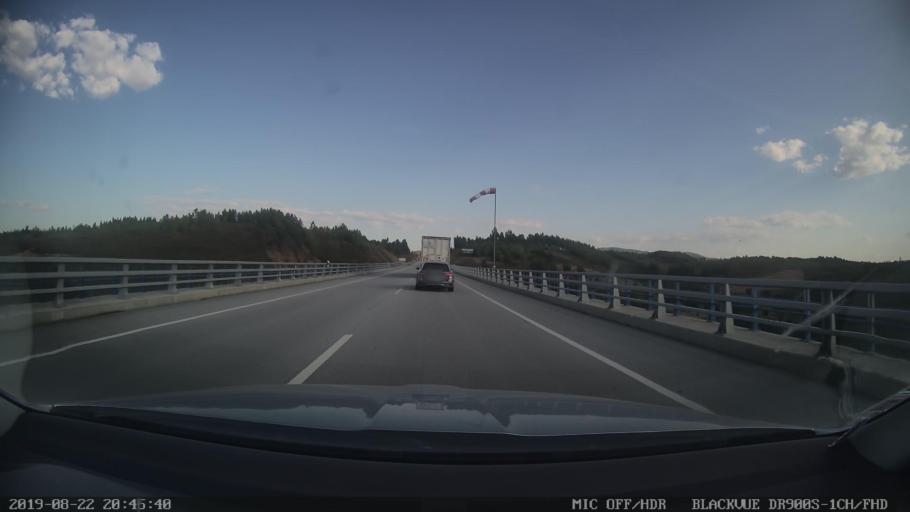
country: PT
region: Castelo Branco
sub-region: Proenca-A-Nova
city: Proenca-a-Nova
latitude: 39.7192
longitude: -7.8688
